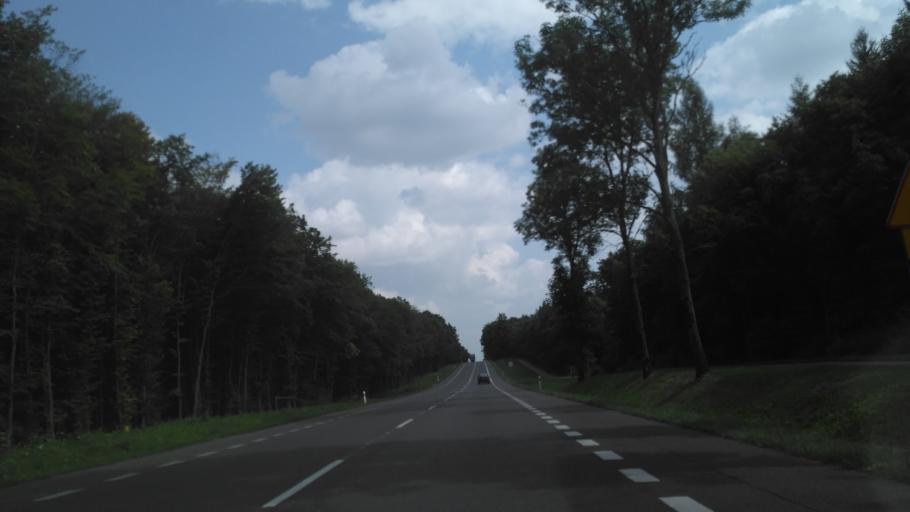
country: PL
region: Lublin Voivodeship
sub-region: Chelm
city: Chelm
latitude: 51.1560
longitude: 23.4078
